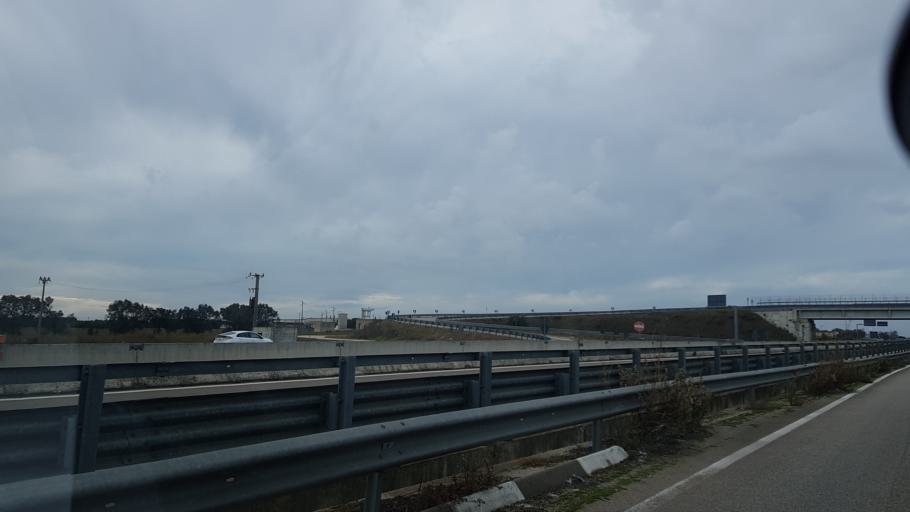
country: IT
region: Apulia
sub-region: Provincia di Brindisi
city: Mesagne
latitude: 40.5765
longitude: 17.8347
